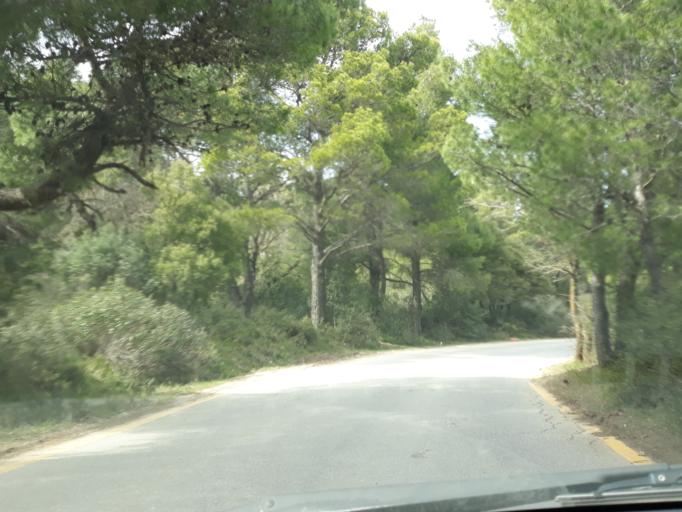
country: GR
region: Attica
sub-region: Nomarchia Anatolikis Attikis
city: Varybobi
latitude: 38.1740
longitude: 23.7909
